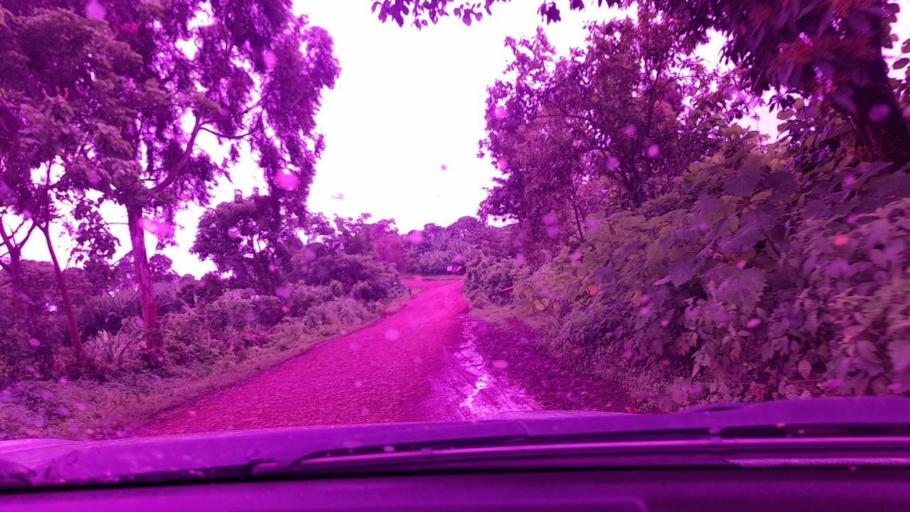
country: ET
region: Southern Nations, Nationalities, and People's Region
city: Tippi
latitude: 7.5719
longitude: 35.6460
